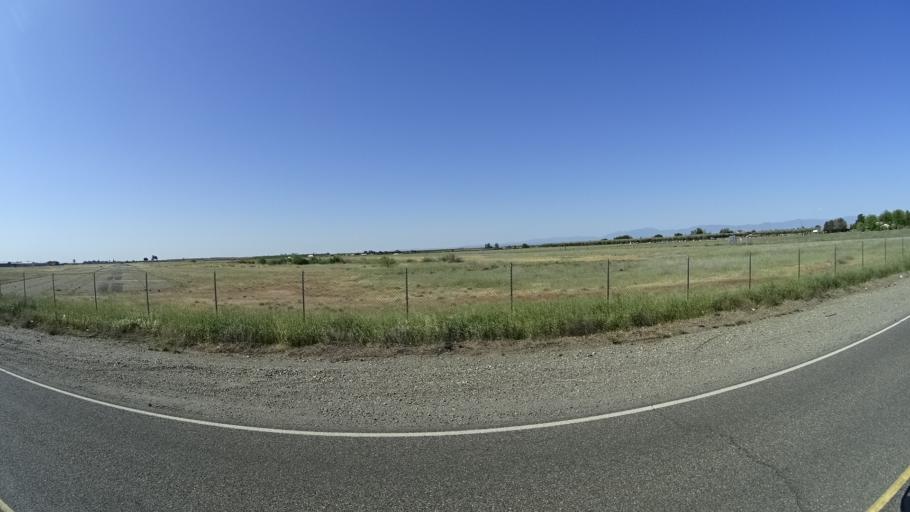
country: US
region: California
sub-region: Glenn County
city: Orland
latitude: 39.7281
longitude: -122.1488
